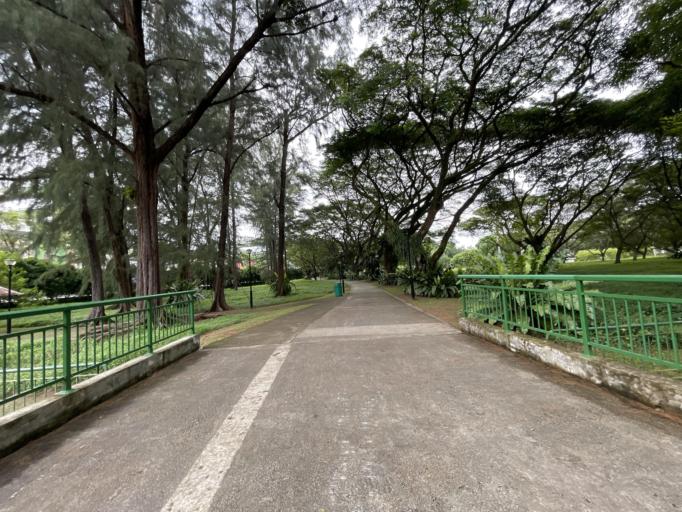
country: SG
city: Singapore
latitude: 1.2879
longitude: 103.7725
